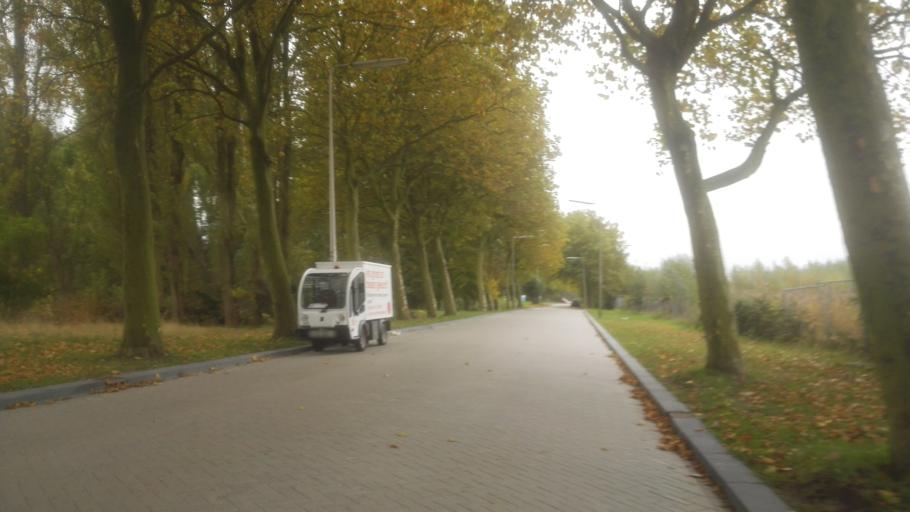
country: NL
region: South Holland
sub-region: Gemeente Delft
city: Delft
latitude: 51.9875
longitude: 4.3855
